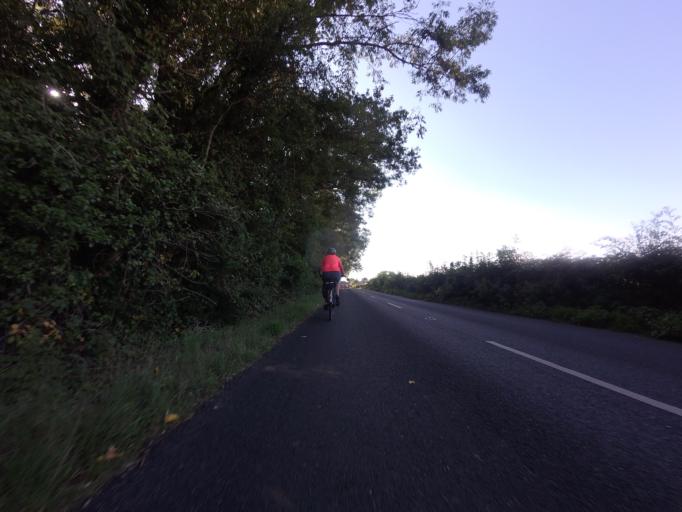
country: GB
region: England
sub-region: Kent
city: Tenterden
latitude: 51.0617
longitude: 0.6895
